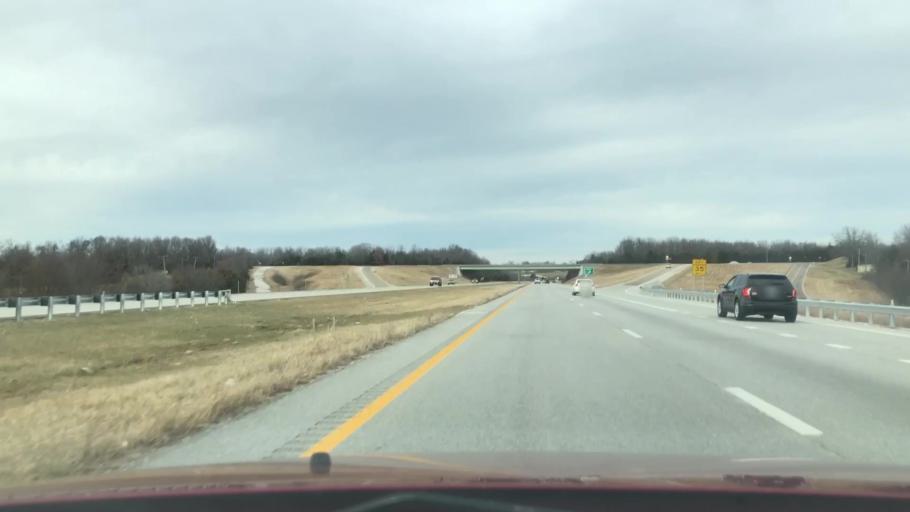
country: US
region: Missouri
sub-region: Greene County
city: Springfield
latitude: 37.2563
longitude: -93.2244
